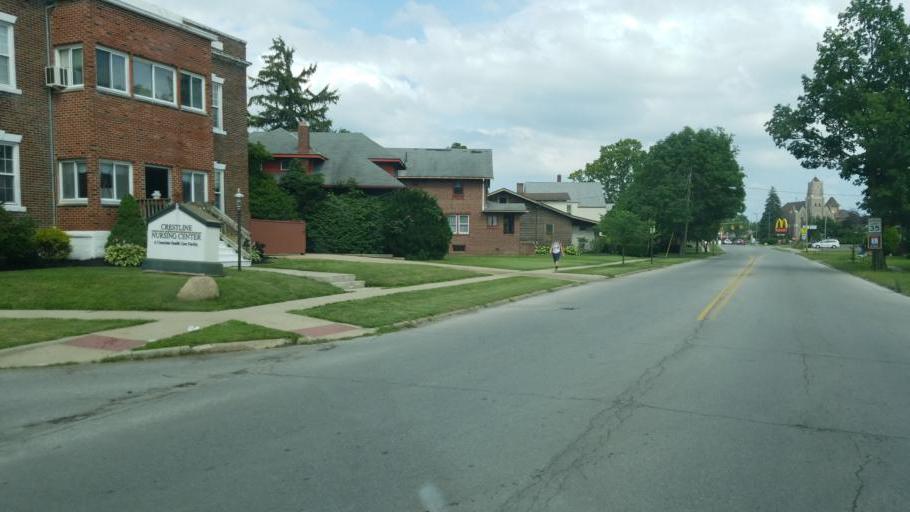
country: US
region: Ohio
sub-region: Crawford County
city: Crestline
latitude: 40.7890
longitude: -82.7410
